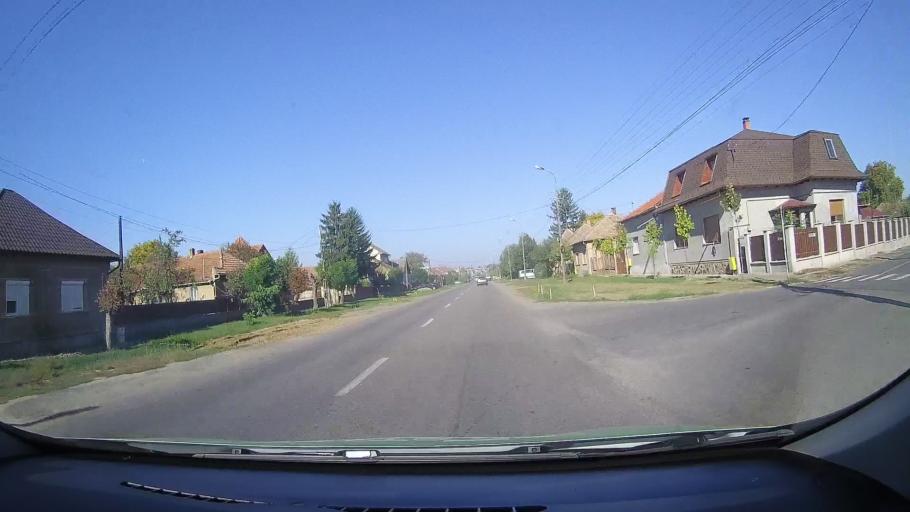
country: RO
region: Satu Mare
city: Carei
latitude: 47.6766
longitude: 22.4773
